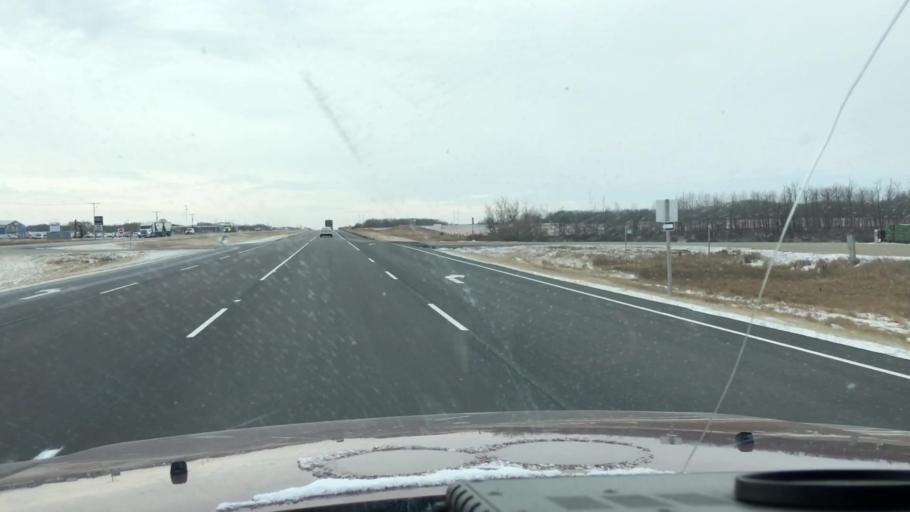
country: CA
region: Saskatchewan
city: Saskatoon
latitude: 51.9698
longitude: -106.5540
